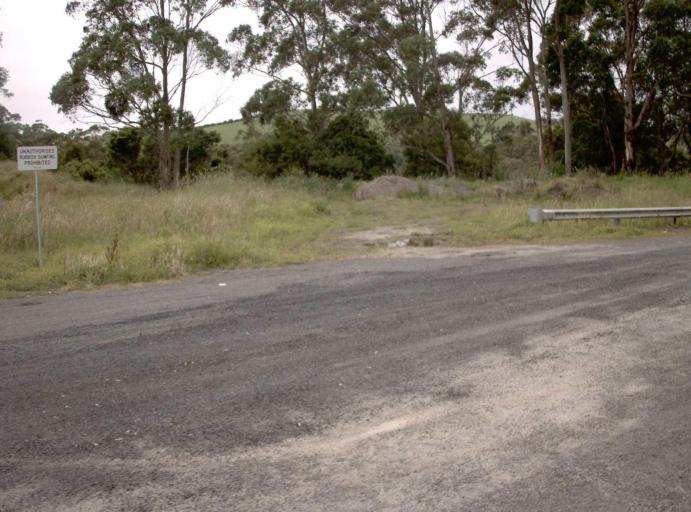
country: AU
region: Victoria
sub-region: Bass Coast
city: North Wonthaggi
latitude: -38.5561
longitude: 145.9538
